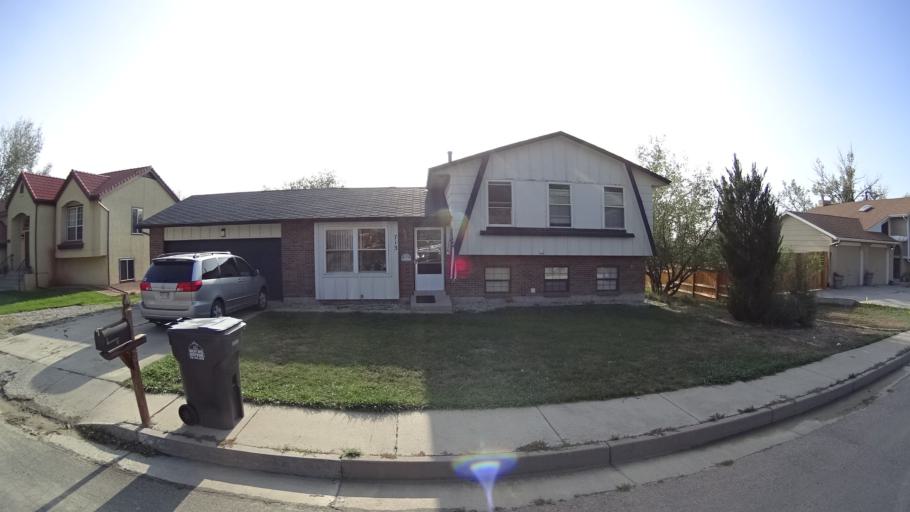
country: US
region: Colorado
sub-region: El Paso County
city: Colorado Springs
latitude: 38.8163
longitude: -104.8513
